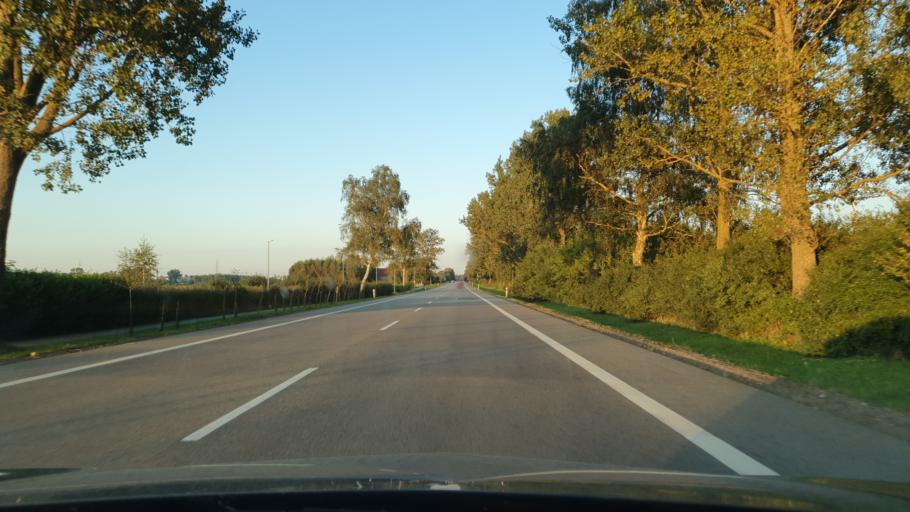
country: PL
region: Pomeranian Voivodeship
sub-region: Powiat slupski
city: Potegowo
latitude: 54.4700
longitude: 17.4754
